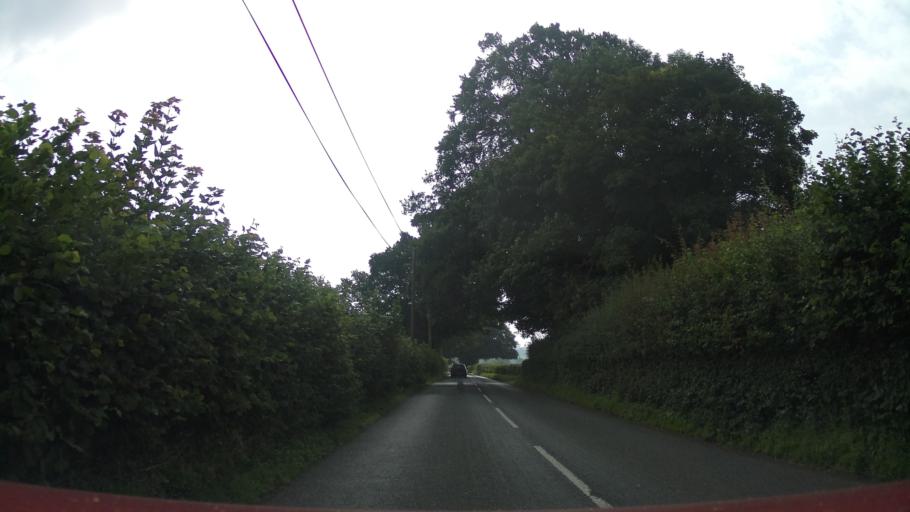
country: GB
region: England
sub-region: Bath and North East Somerset
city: East Harptree
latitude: 51.3020
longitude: -2.6131
